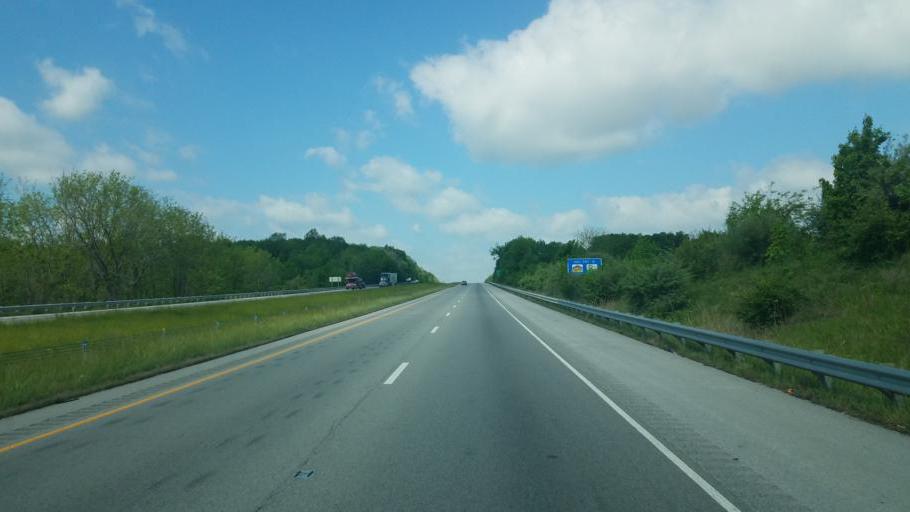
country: US
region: Indiana
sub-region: Putnam County
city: Cloverdale
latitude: 39.5352
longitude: -86.7812
